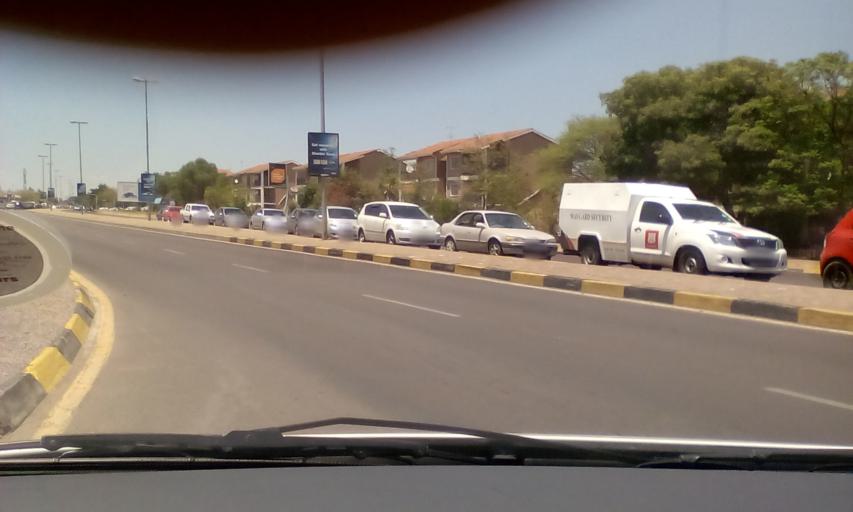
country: BW
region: South East
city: Gaborone
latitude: -24.6515
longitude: 25.9024
